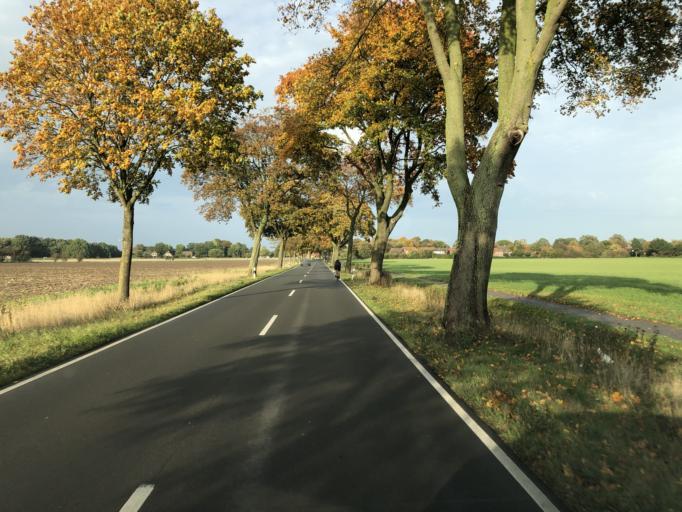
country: DE
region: Lower Saxony
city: Neu Wulmstorf
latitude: 53.4326
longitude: 9.7988
